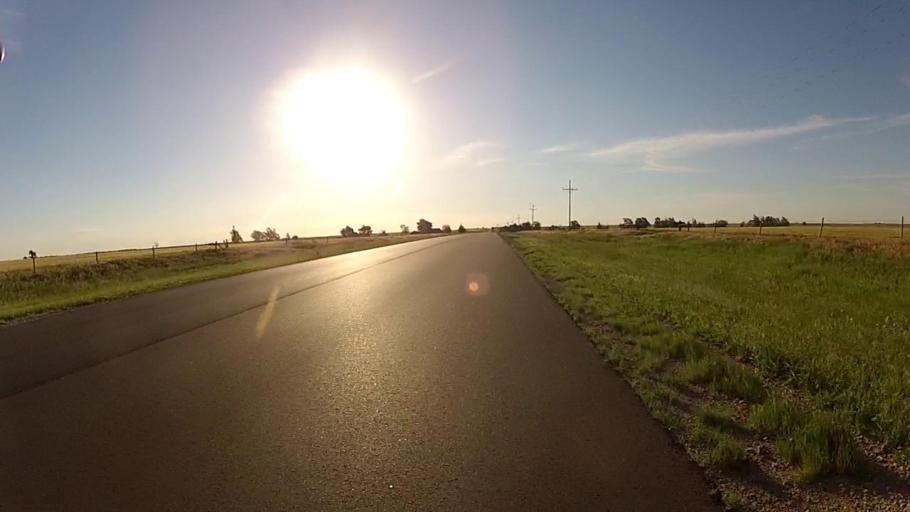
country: US
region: Kansas
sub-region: Comanche County
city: Coldwater
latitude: 37.2815
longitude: -99.1771
